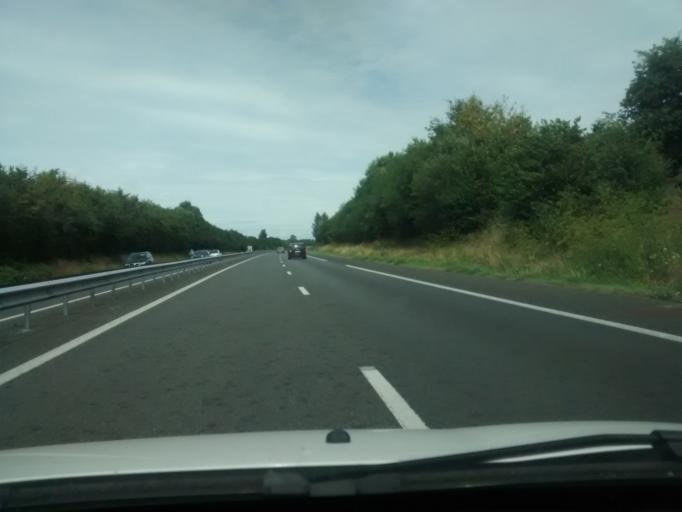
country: FR
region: Brittany
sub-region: Departement d'Ille-et-Vilaine
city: Saint-Etienne-en-Cogles
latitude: 48.4537
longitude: -1.3271
